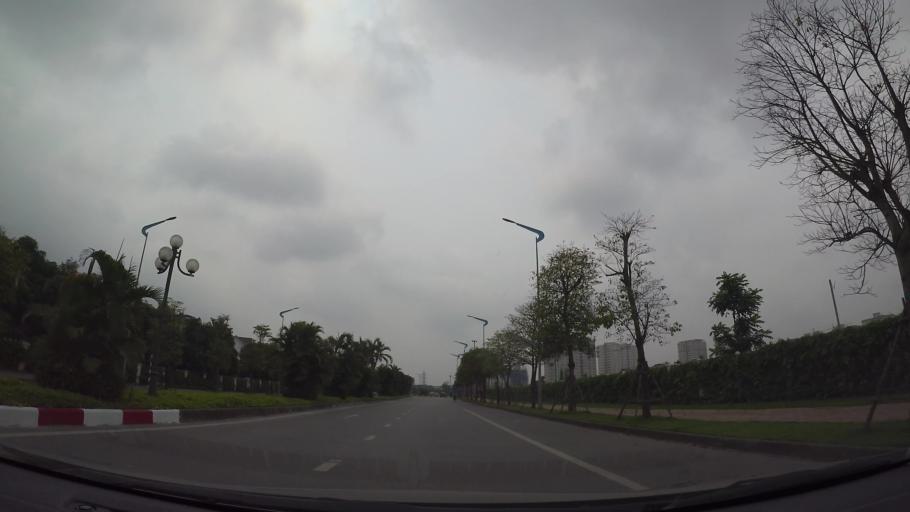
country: VN
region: Ha Noi
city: Trau Quy
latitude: 21.0437
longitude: 105.9118
